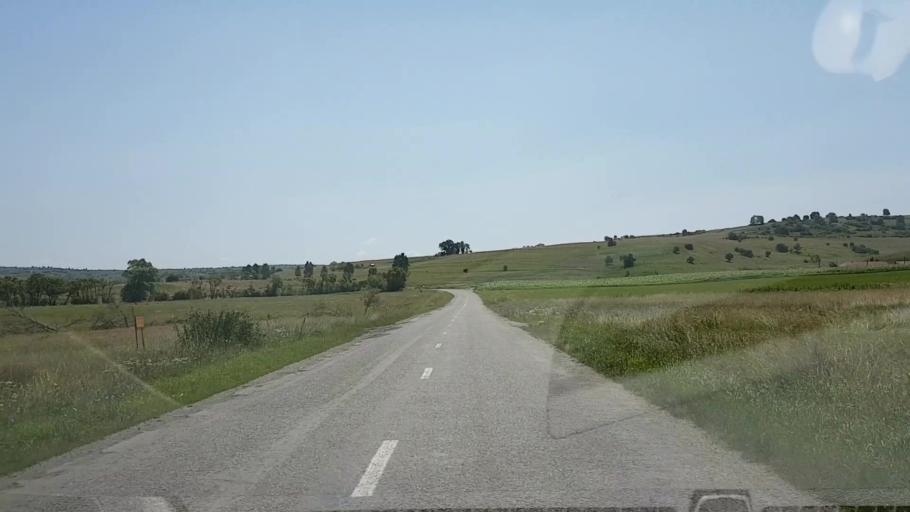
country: RO
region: Sibiu
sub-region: Comuna Merghindeal
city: Merghindeal
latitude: 45.9587
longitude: 24.7595
